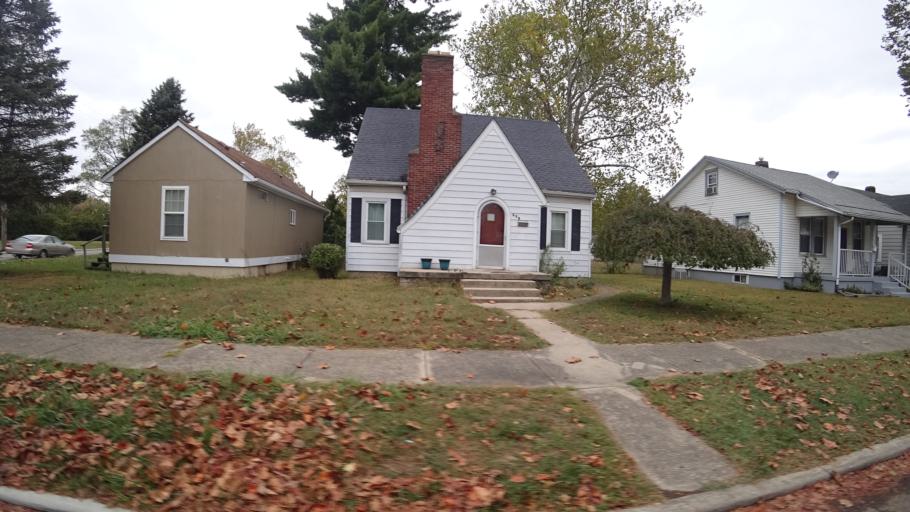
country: US
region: Ohio
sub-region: Butler County
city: Fairfield
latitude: 39.3663
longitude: -84.5629
